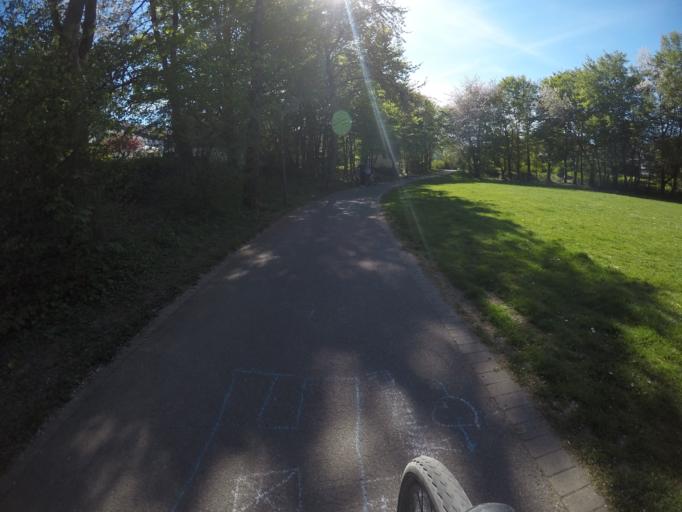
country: DE
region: Baden-Wuerttemberg
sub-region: Regierungsbezirk Stuttgart
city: Kornwestheim
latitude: 48.8609
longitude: 9.2058
